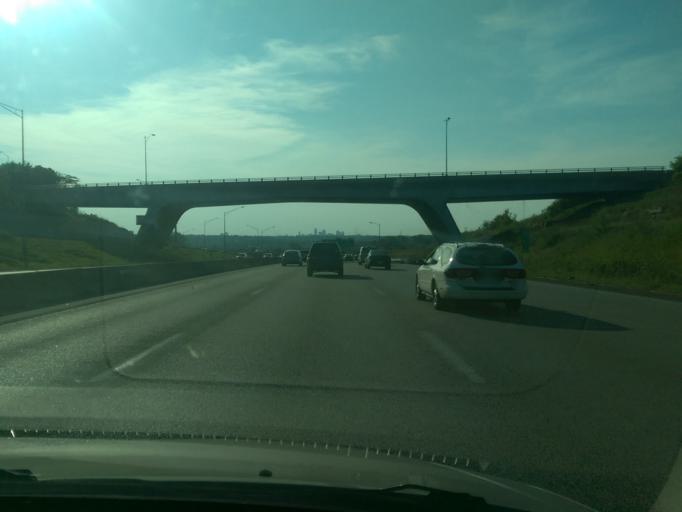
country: US
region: Missouri
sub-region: Jackson County
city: Raytown
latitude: 39.0551
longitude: -94.4814
